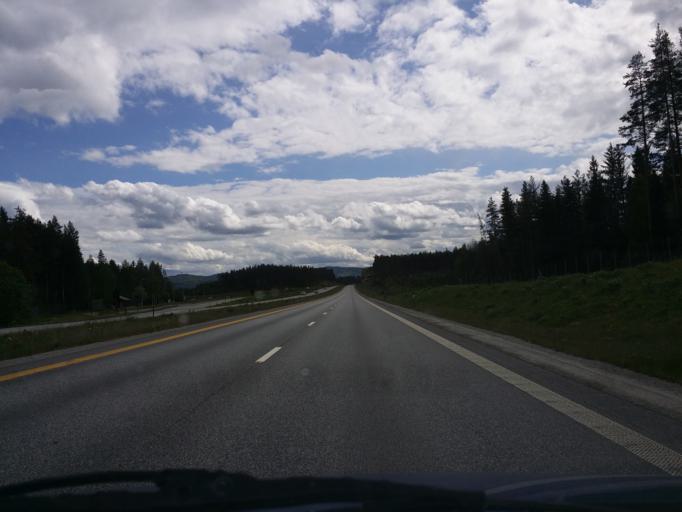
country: NO
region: Hedmark
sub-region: Stange
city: Stange
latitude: 60.6812
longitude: 11.2843
